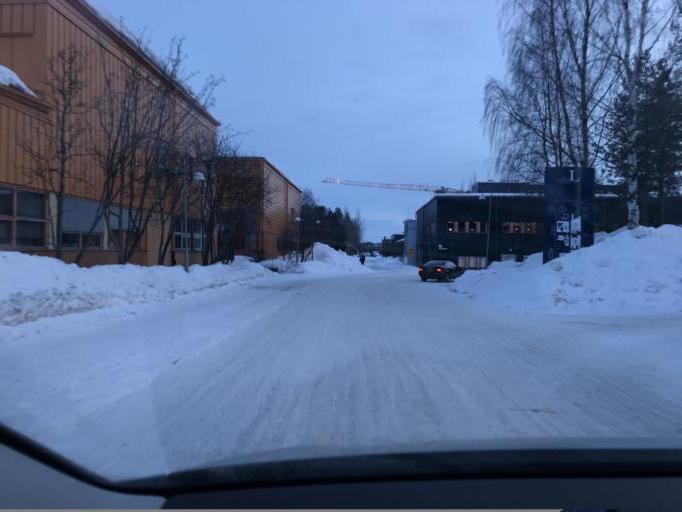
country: SE
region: Norrbotten
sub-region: Lulea Kommun
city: Lulea
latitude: 65.6200
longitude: 22.1405
